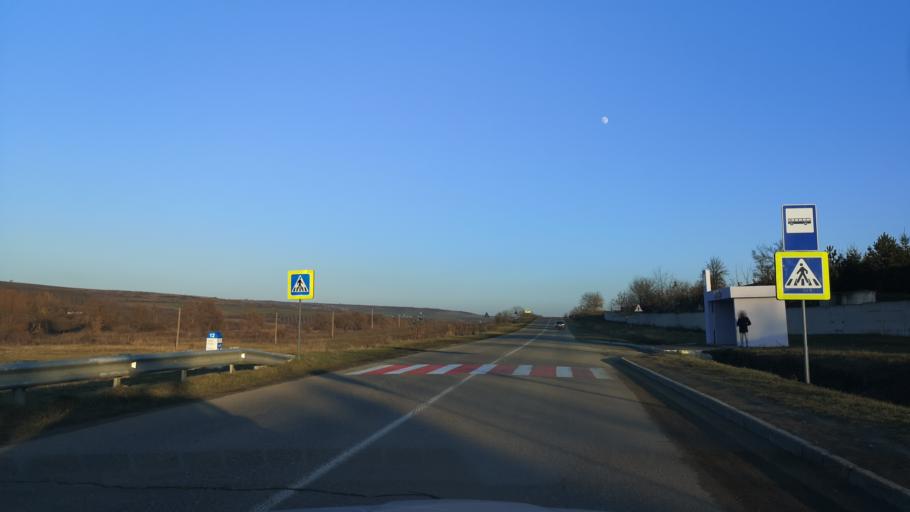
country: MD
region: Orhei
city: Orhei
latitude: 47.3400
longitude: 28.6578
